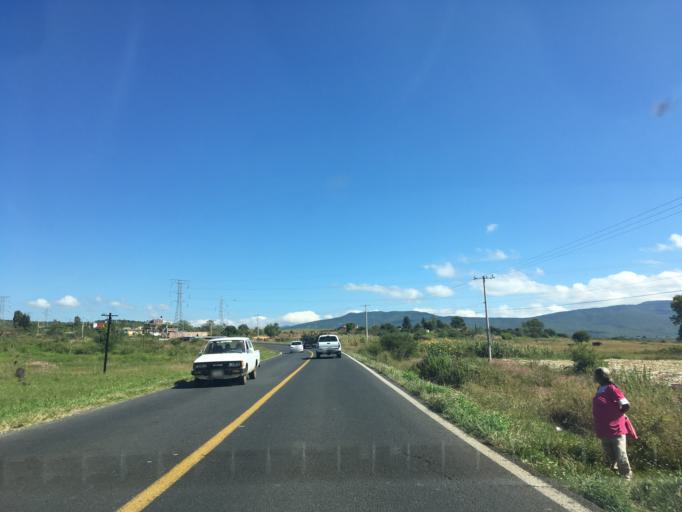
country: MX
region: Mexico
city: Tlazazalca
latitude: 19.9833
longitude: -102.0595
